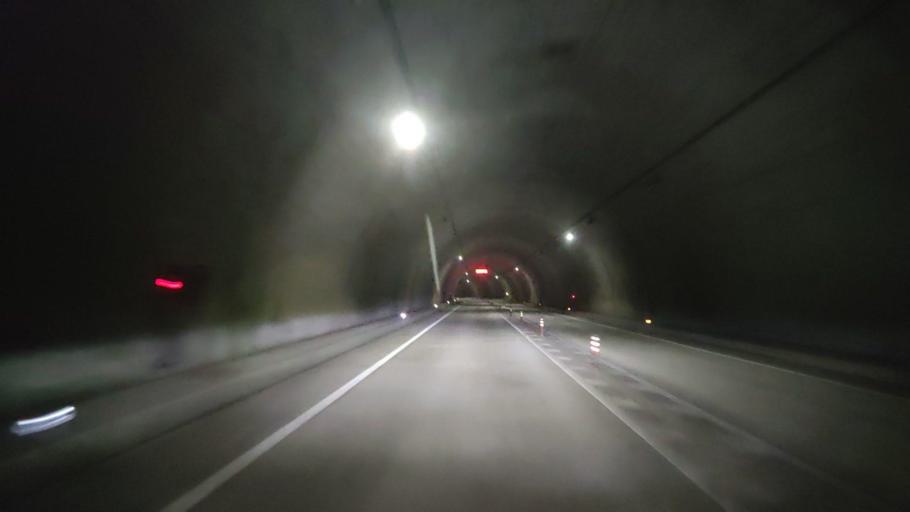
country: JP
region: Wakayama
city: Shingu
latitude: 33.7201
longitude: 135.9761
